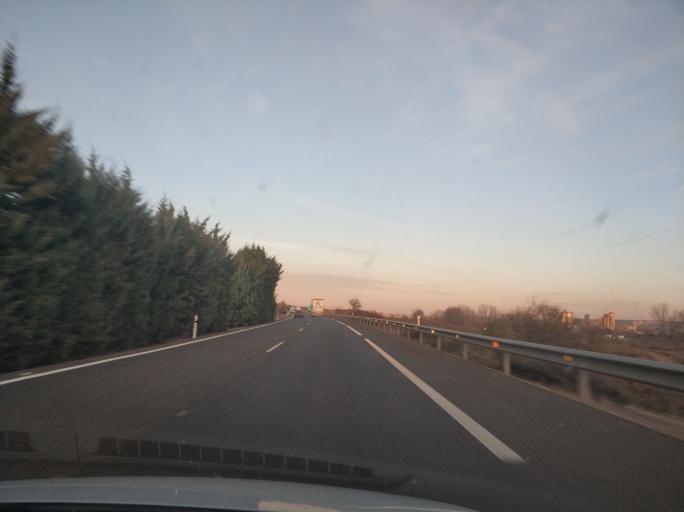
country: ES
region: Castille and Leon
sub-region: Provincia de Palencia
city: Venta de Banos
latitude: 41.9394
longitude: -4.4891
